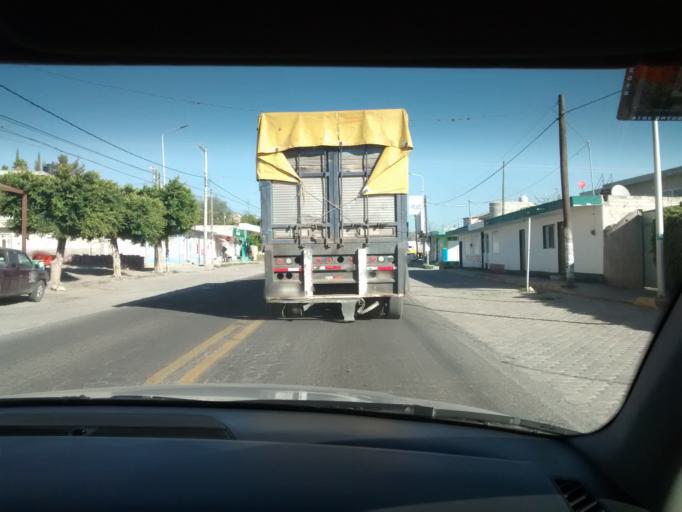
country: MX
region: Puebla
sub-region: Tepanco de Lopez
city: San Andres Cacaloapan
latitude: 18.5560
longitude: -97.5624
